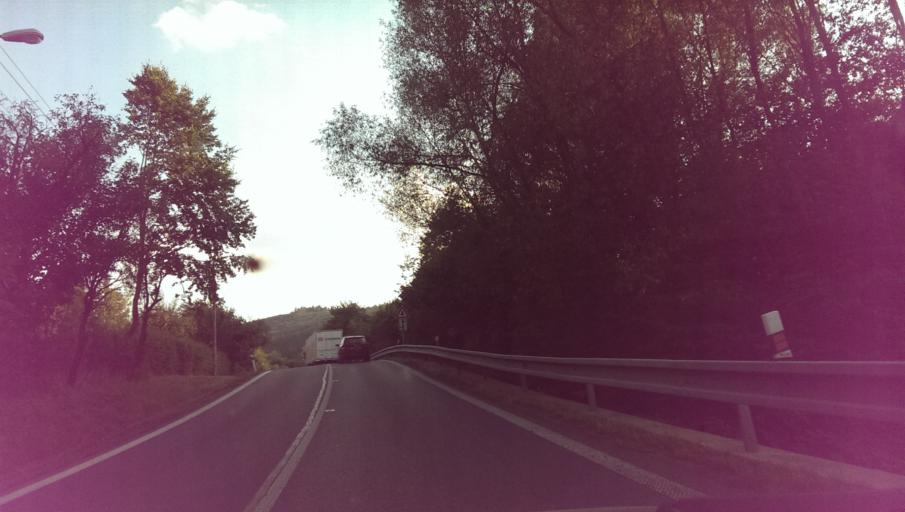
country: CZ
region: Zlin
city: Slusovice
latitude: 49.2044
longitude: 17.8037
